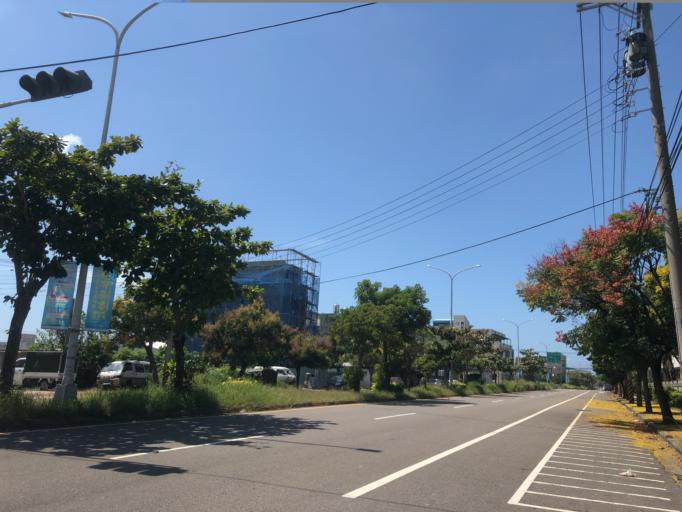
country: TW
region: Taiwan
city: Fengyuan
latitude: 24.2786
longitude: 120.5573
